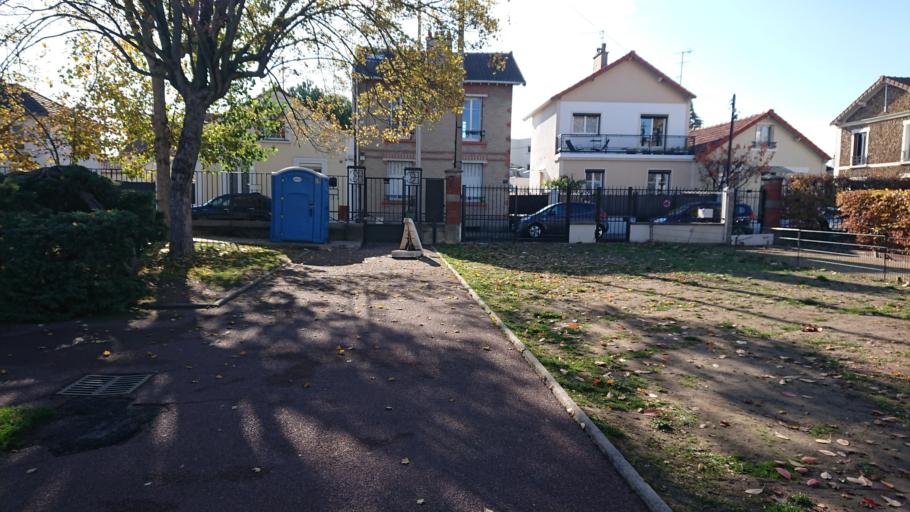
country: FR
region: Ile-de-France
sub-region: Departement des Hauts-de-Seine
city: Bois-Colombes
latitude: 48.9243
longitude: 2.2719
